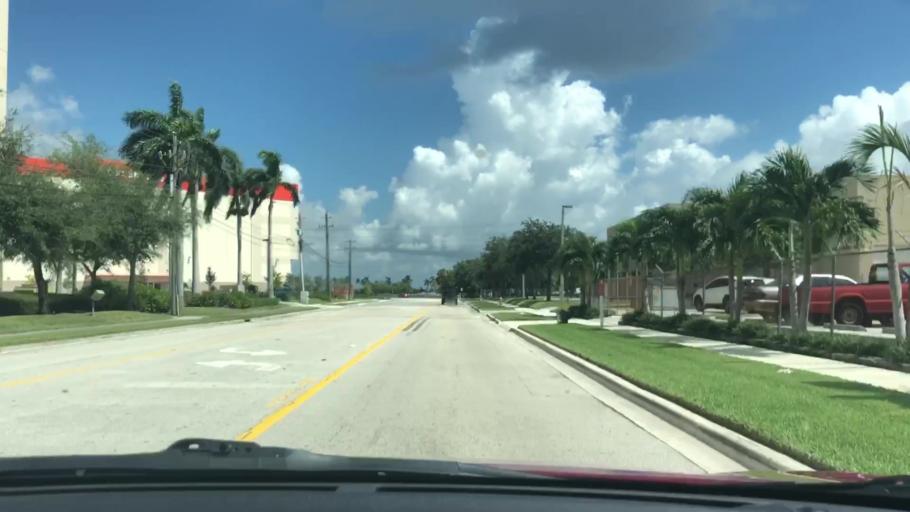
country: US
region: Florida
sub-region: Palm Beach County
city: West Palm Beach
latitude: 26.7003
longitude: -80.0676
